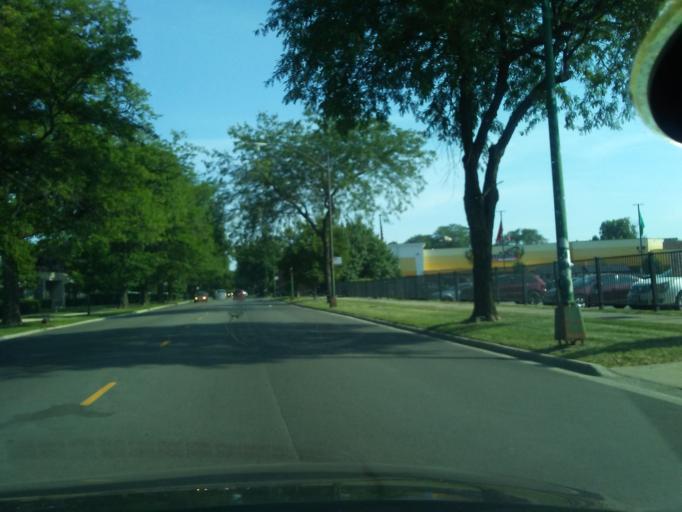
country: US
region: Illinois
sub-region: Cook County
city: Evanston
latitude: 42.0036
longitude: -87.6795
